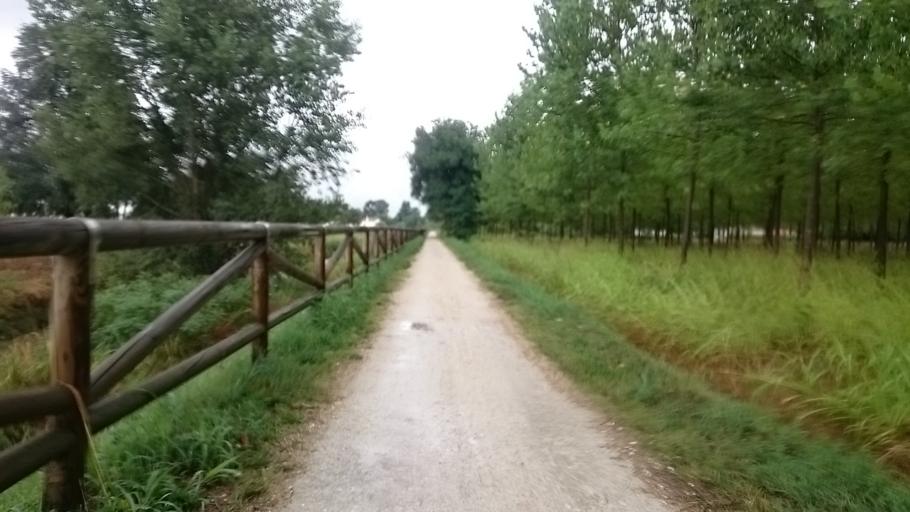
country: IT
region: Veneto
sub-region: Provincia di Treviso
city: Castelfranco Veneto
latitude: 45.6648
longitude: 11.9225
